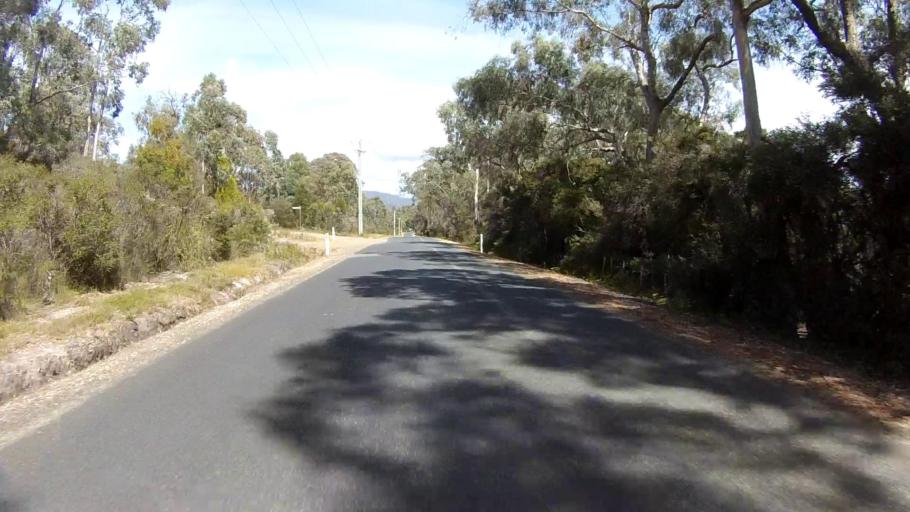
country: AU
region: Tasmania
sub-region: Huon Valley
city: Cygnet
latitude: -43.2449
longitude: 147.1108
